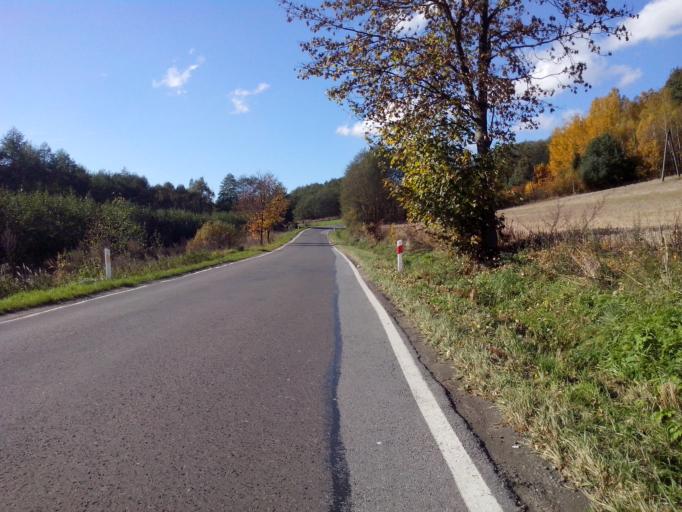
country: PL
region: Subcarpathian Voivodeship
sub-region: Powiat krosnienski
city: Korczyna
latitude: 49.7654
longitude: 21.8292
